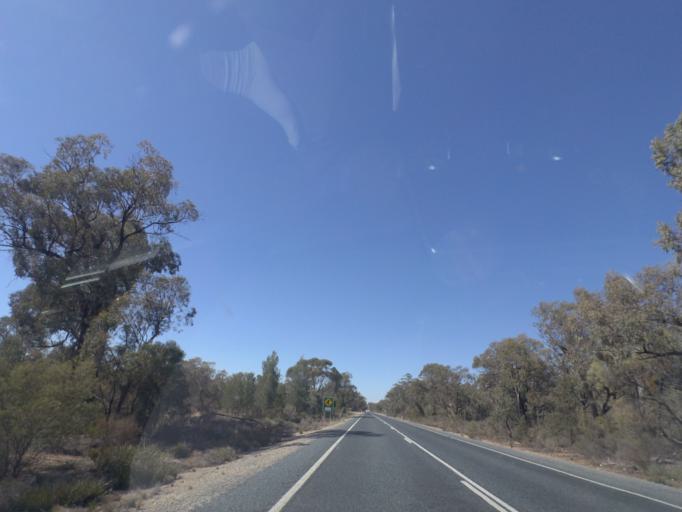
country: AU
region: New South Wales
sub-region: Bland
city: West Wyalong
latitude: -34.1407
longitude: 147.1202
